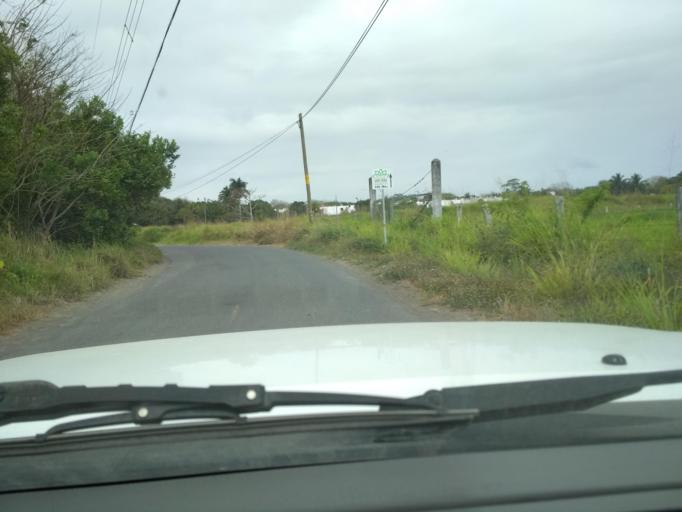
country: MX
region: Veracruz
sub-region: Medellin
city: Fraccionamiento Arboledas San Ramon
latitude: 19.0899
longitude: -96.1338
